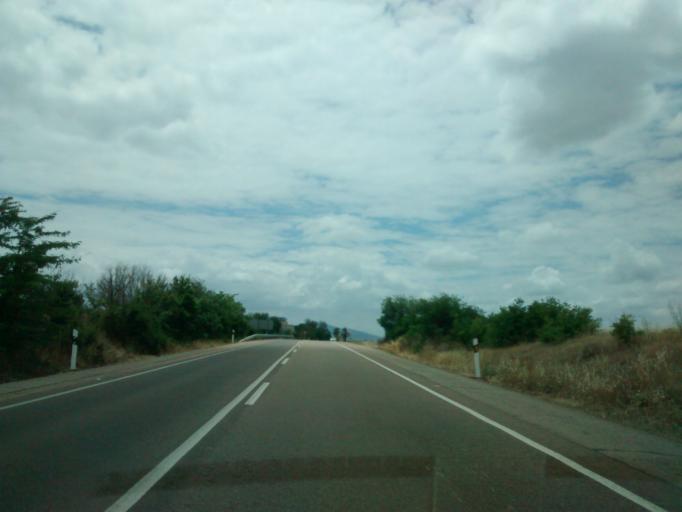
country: ES
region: Extremadura
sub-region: Provincia de Badajoz
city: Merida
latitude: 38.9319
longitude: -6.3128
